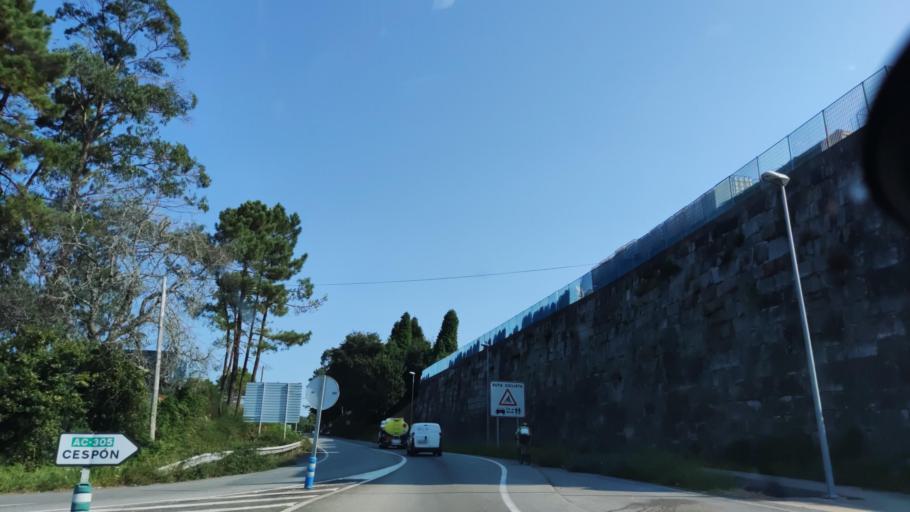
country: ES
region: Galicia
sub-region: Provincia da Coruna
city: Boiro
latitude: 42.6637
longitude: -8.8707
